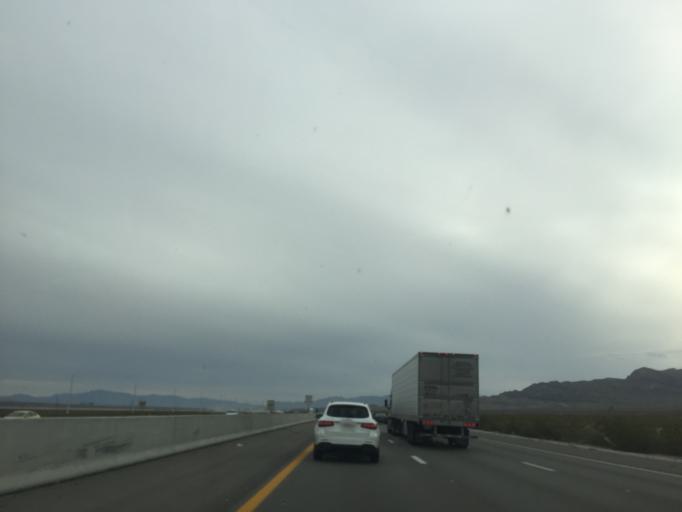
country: US
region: Nevada
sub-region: Clark County
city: Sandy Valley
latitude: 35.7005
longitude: -115.3704
